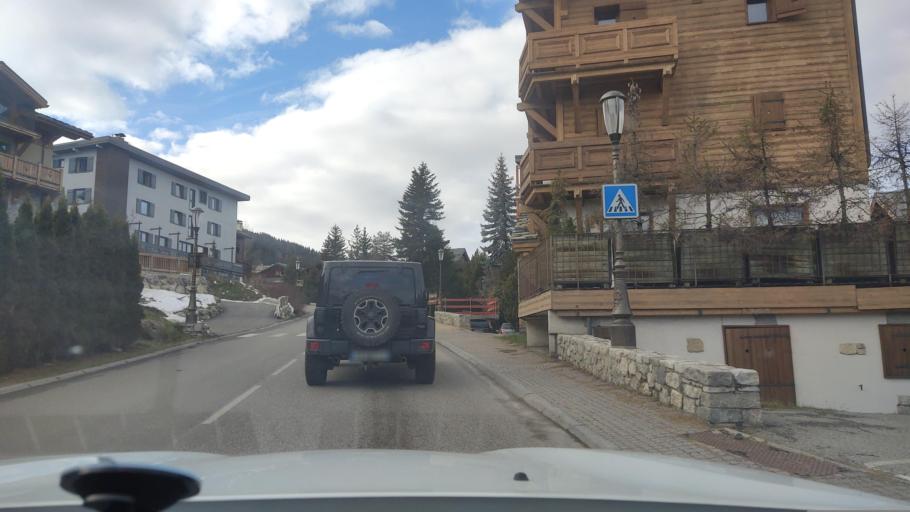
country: FR
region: Rhone-Alpes
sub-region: Departement de la Savoie
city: Saint-Bon-Tarentaise
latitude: 45.4339
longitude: 6.6249
